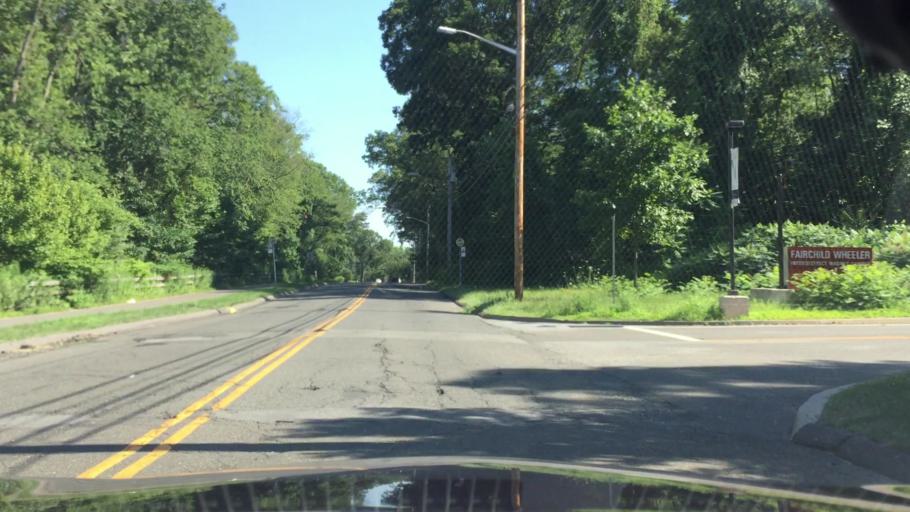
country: US
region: Connecticut
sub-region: Fairfield County
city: Trumbull
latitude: 41.2271
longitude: -73.1814
